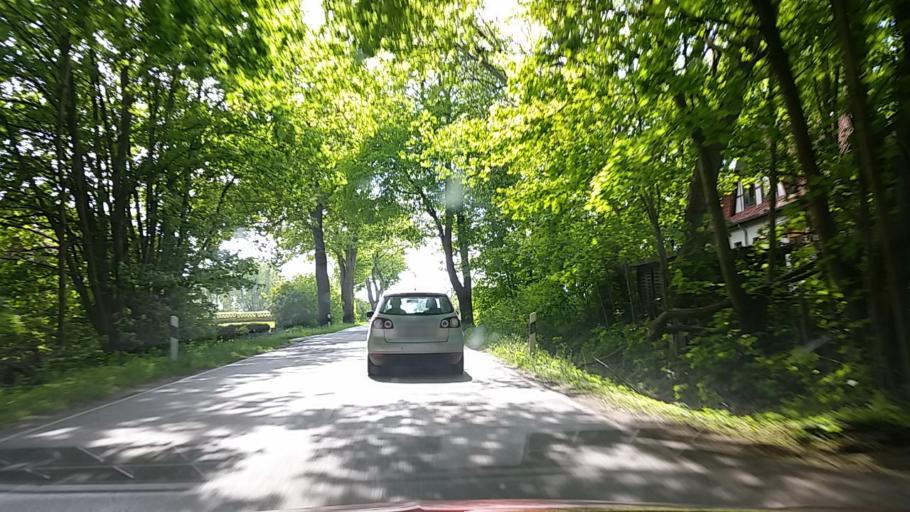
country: DE
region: Schleswig-Holstein
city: Reinfeld
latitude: 53.8235
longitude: 10.4865
